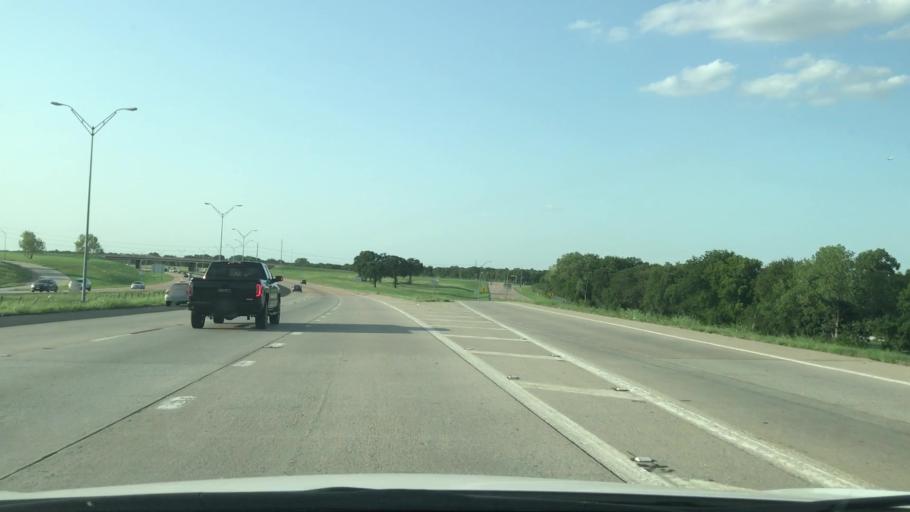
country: US
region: Texas
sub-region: Tarrant County
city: Euless
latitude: 32.8618
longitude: -97.0642
